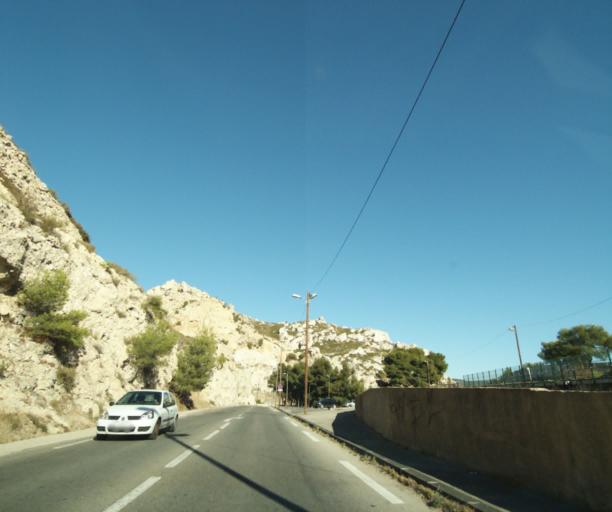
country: FR
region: Provence-Alpes-Cote d'Azur
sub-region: Departement des Bouches-du-Rhone
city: Le Rove
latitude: 43.3566
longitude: 5.2863
